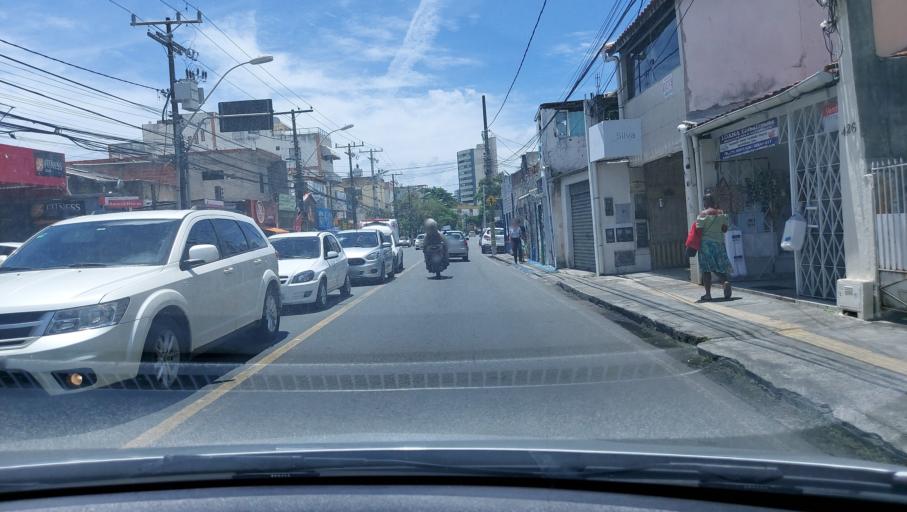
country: BR
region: Bahia
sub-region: Salvador
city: Salvador
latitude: -12.9893
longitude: -38.4825
